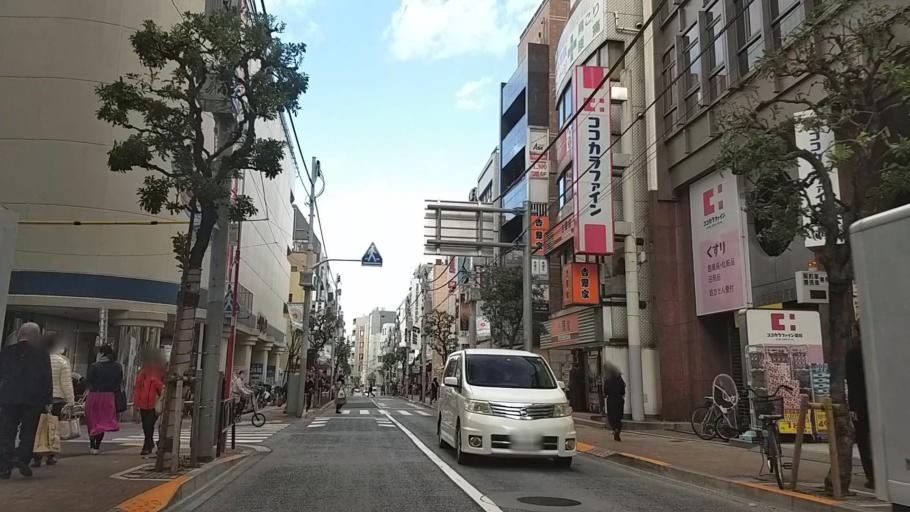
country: JP
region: Tokyo
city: Tokyo
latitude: 35.6443
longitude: 139.6708
